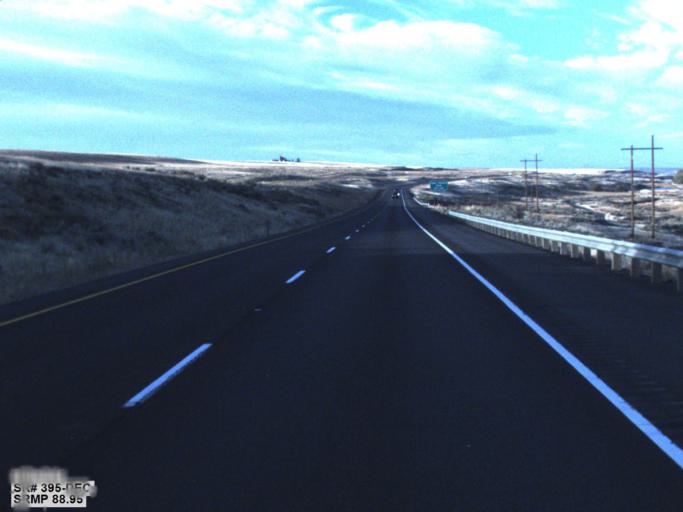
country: US
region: Washington
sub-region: Adams County
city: Ritzville
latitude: 47.0325
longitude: -118.4630
